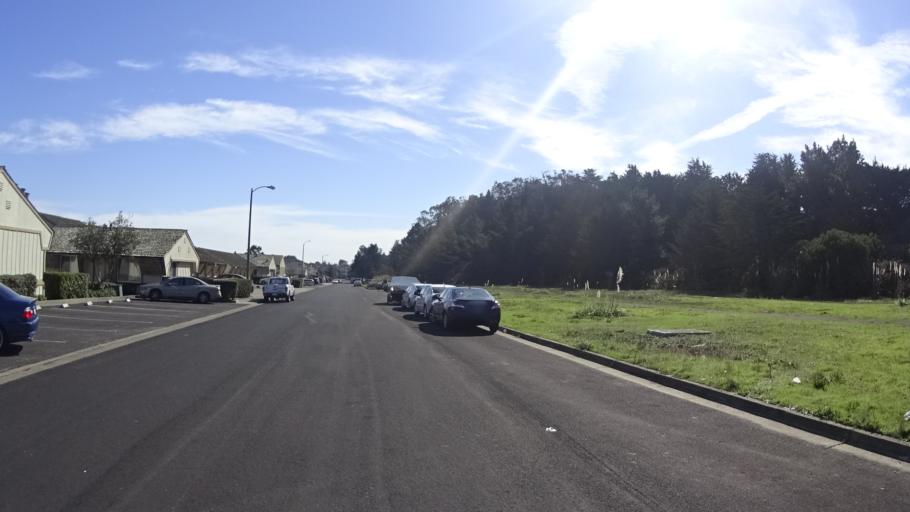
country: US
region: California
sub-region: San Mateo County
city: Colma
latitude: 37.6441
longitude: -122.4678
